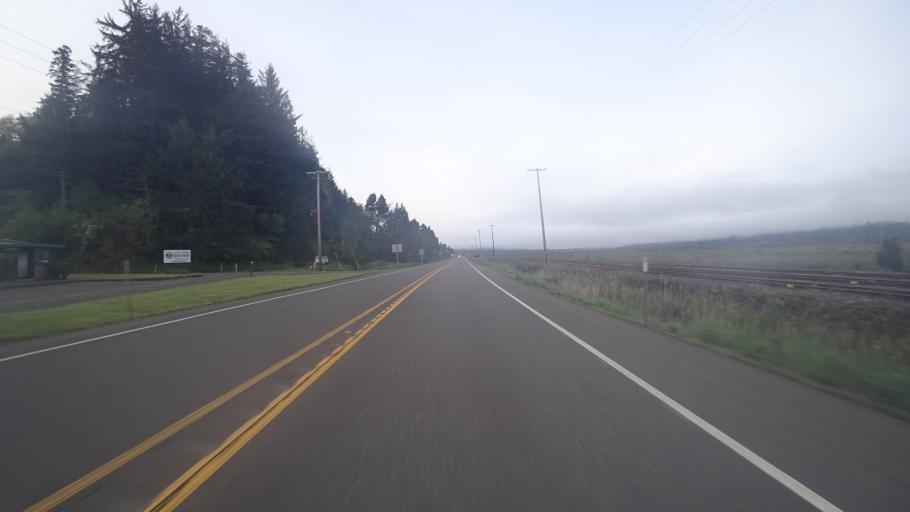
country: US
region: Oregon
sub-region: Douglas County
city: Reedsport
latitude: 43.7389
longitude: -124.1110
